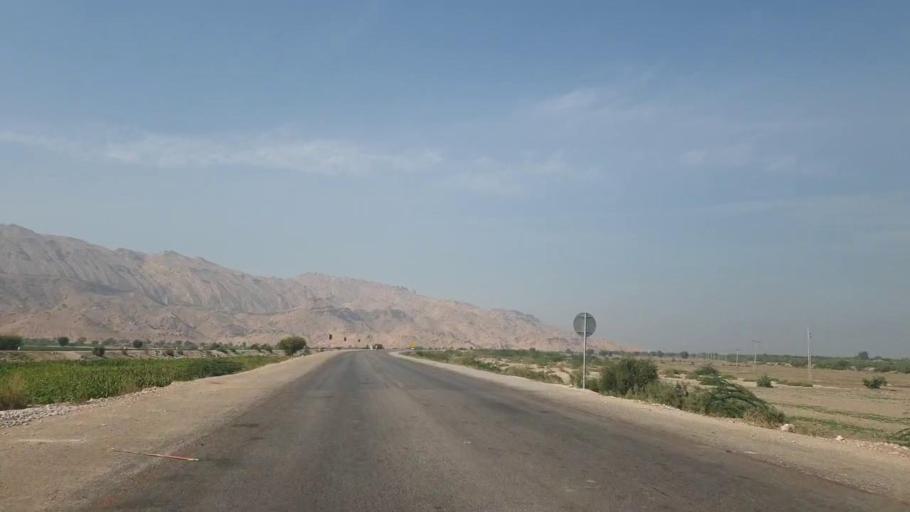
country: PK
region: Sindh
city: Sehwan
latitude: 26.2739
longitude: 67.9001
